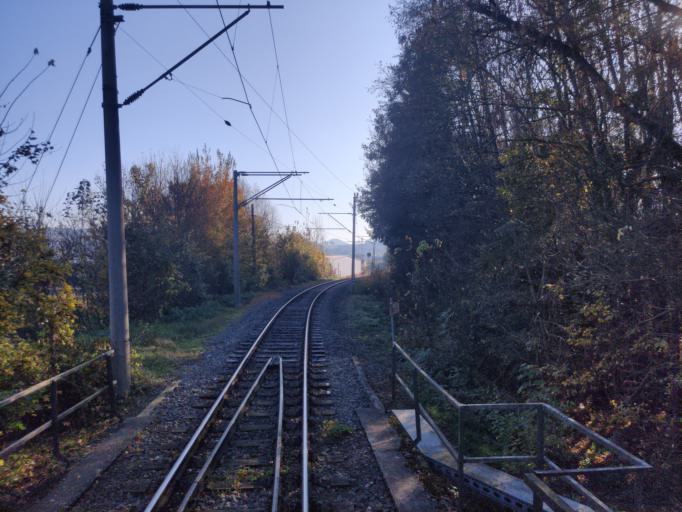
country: AT
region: Styria
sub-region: Politischer Bezirk Suedoststeiermark
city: Feldbach
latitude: 46.9562
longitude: 15.8983
